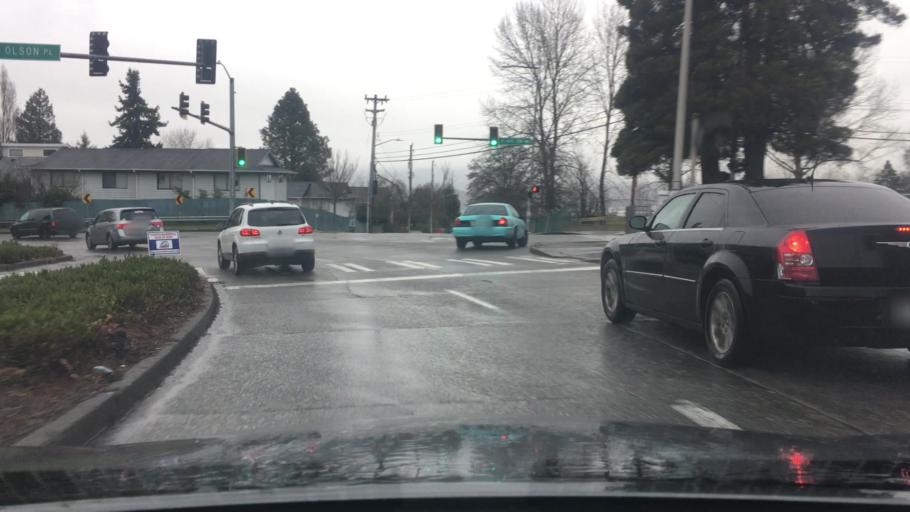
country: US
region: Washington
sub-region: King County
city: White Center
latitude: 47.5172
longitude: -122.3406
